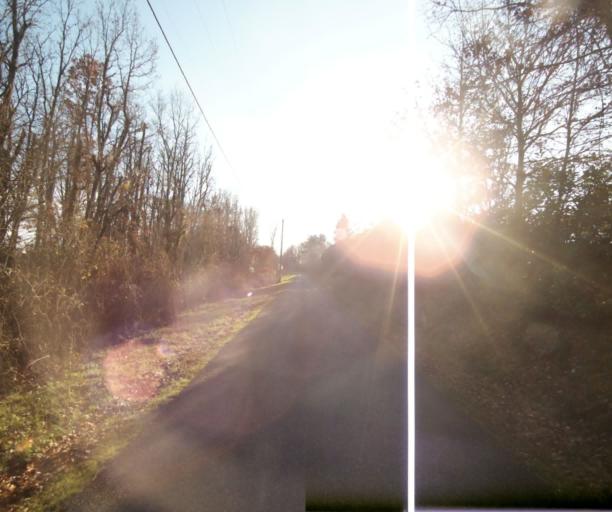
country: FR
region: Midi-Pyrenees
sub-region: Departement du Tarn-et-Garonne
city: Moissac
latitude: 44.1465
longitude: 1.1133
